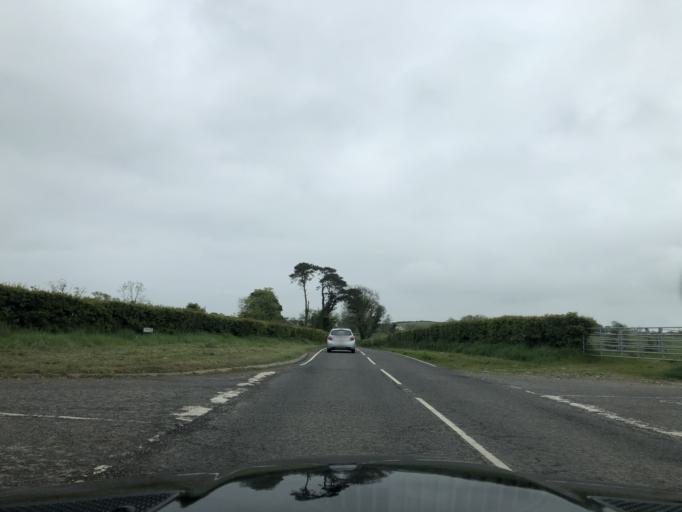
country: GB
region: Northern Ireland
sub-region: Down District
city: Killyleagh
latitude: 54.3582
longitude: -5.6391
